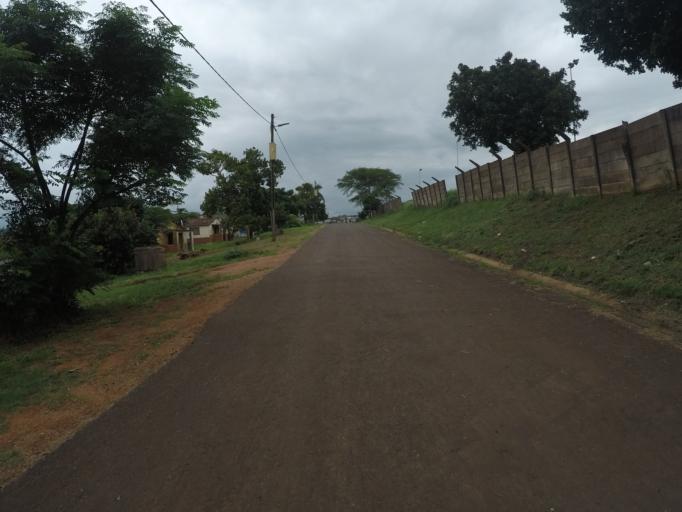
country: ZA
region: KwaZulu-Natal
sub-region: uThungulu District Municipality
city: Empangeni
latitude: -28.7763
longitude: 31.8614
